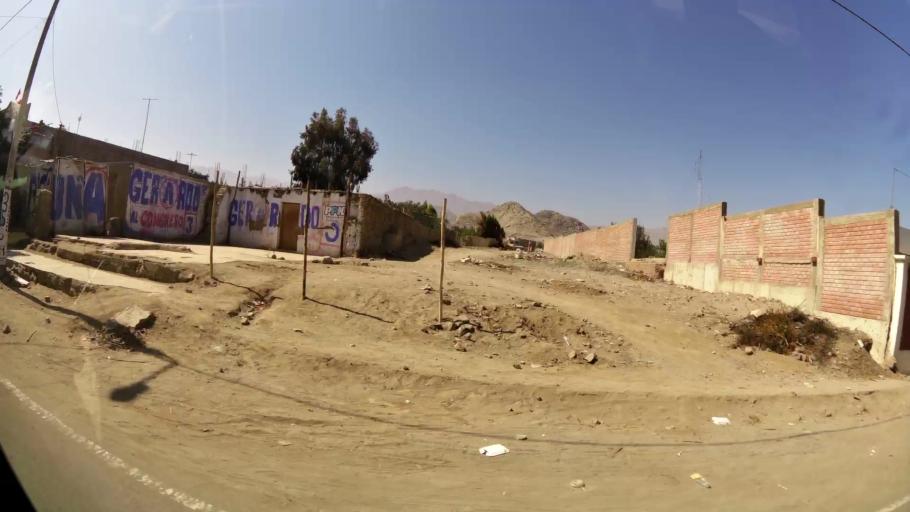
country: PE
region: Ica
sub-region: Provincia de Ica
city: San Juan Bautista
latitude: -13.9367
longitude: -75.6730
